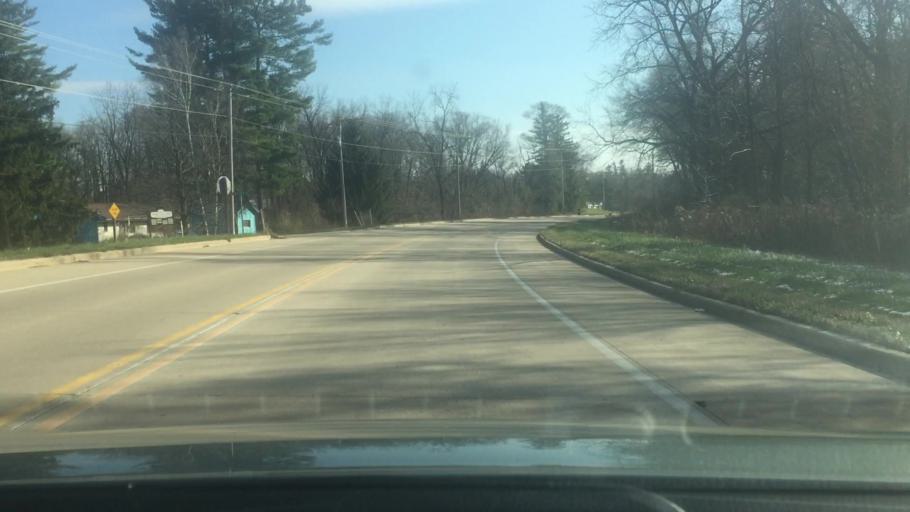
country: US
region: Wisconsin
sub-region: Jefferson County
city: Cambridge
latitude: 42.9986
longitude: -89.0027
